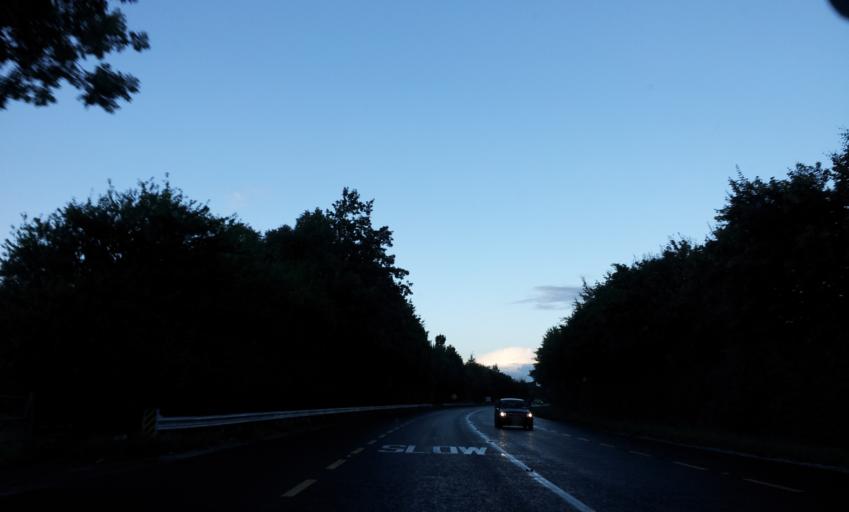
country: IE
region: Munster
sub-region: County Limerick
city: Rathkeale
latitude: 52.5079
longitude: -8.9898
